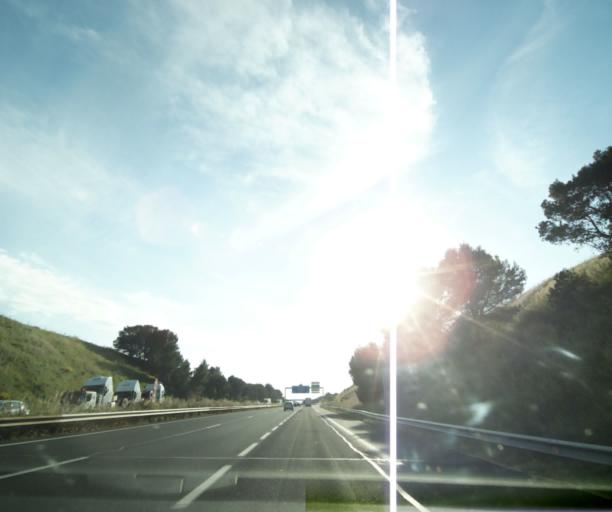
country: FR
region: Languedoc-Roussillon
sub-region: Departement de l'Herault
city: Sauvian
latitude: 43.3044
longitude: 3.2292
